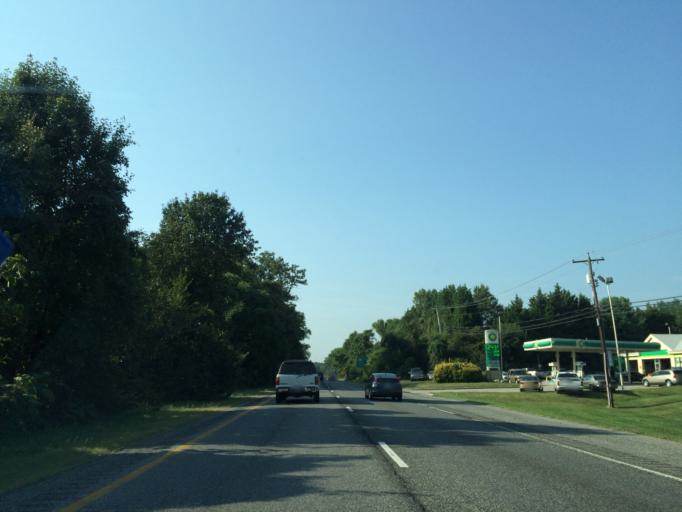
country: US
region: Maryland
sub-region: Prince George's County
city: Mitchellville
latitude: 38.9034
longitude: -76.7196
